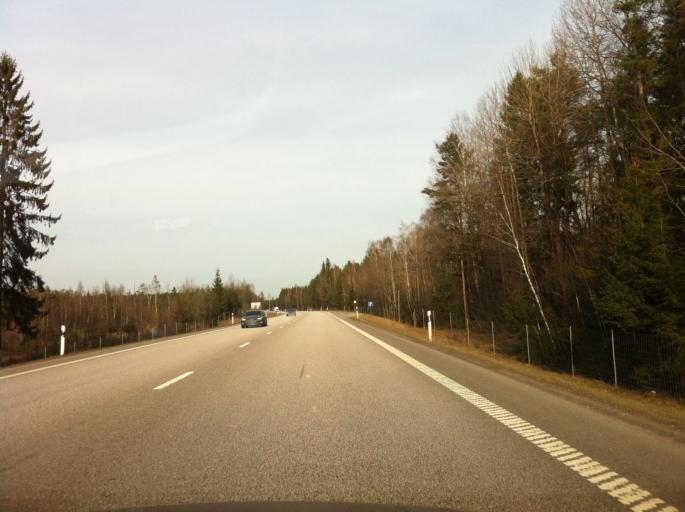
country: SE
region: Vaestra Goetaland
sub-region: Mariestads Kommun
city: Mariestad
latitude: 58.7190
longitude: 13.8818
